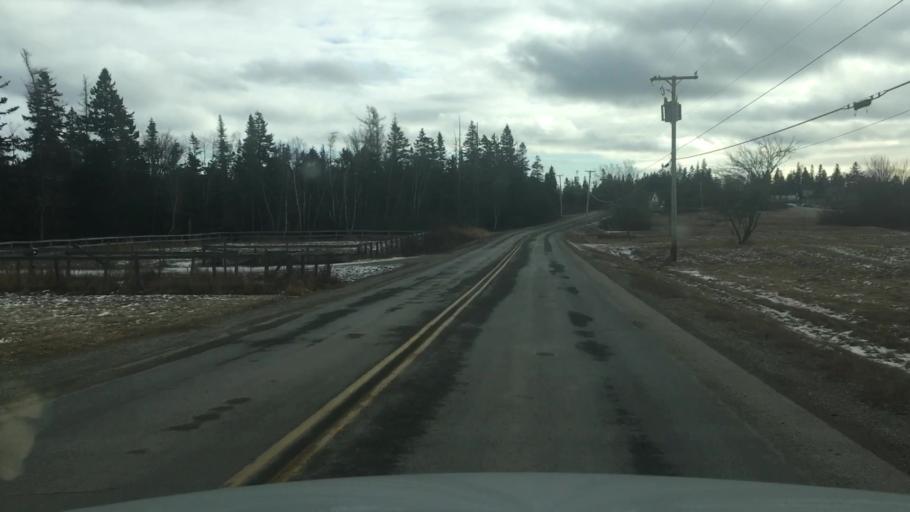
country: US
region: Maine
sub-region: Washington County
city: Machias
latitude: 44.6173
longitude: -67.4796
